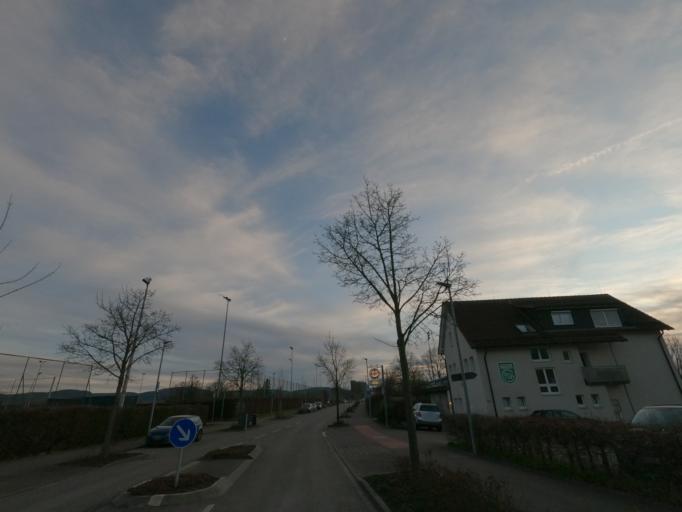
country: DE
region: Baden-Wuerttemberg
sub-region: Regierungsbezirk Stuttgart
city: Goeppingen
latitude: 48.7127
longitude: 9.6769
